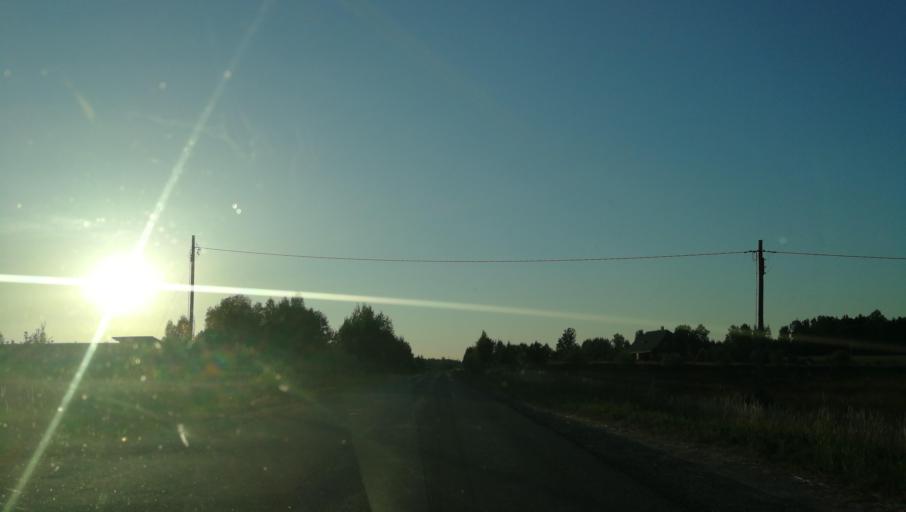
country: LV
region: Cesu Rajons
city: Cesis
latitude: 57.2802
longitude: 25.3178
